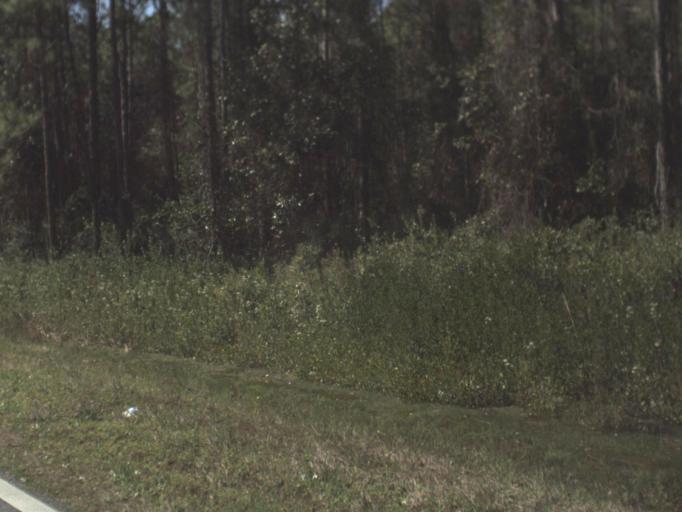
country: US
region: Florida
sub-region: Franklin County
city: Carrabelle
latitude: 29.9134
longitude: -84.5294
